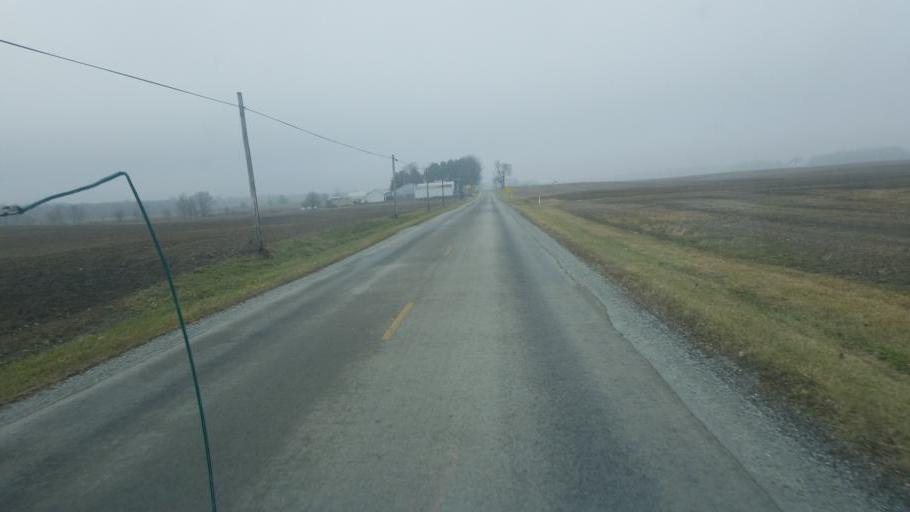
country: US
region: Ohio
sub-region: Hardin County
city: Kenton
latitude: 40.5459
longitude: -83.5142
